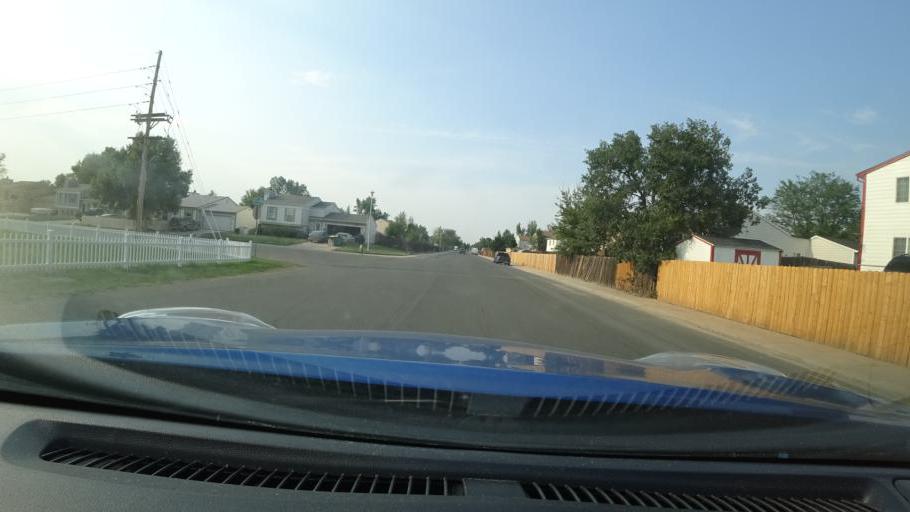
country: US
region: Colorado
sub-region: Adams County
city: Aurora
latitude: 39.7434
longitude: -104.7630
